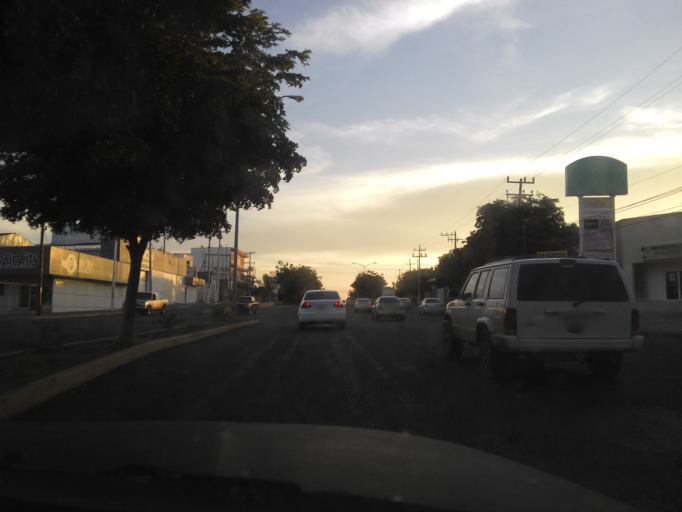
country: MX
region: Sinaloa
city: Culiacan
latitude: 24.7955
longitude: -107.4051
